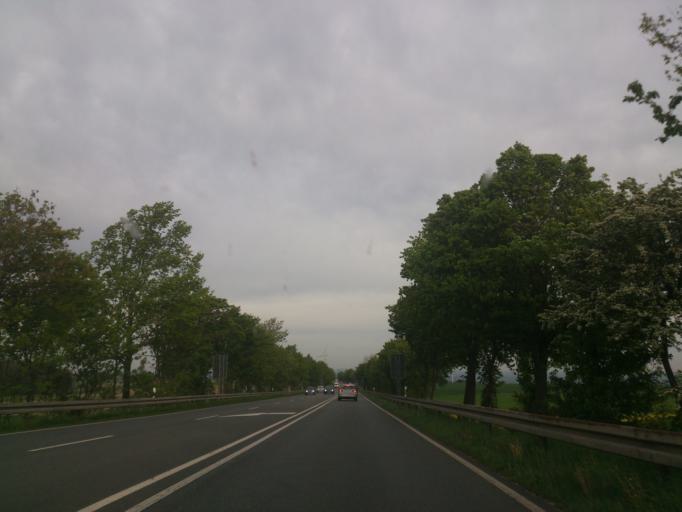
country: DE
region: North Rhine-Westphalia
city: Bad Lippspringe
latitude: 51.7218
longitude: 8.8667
